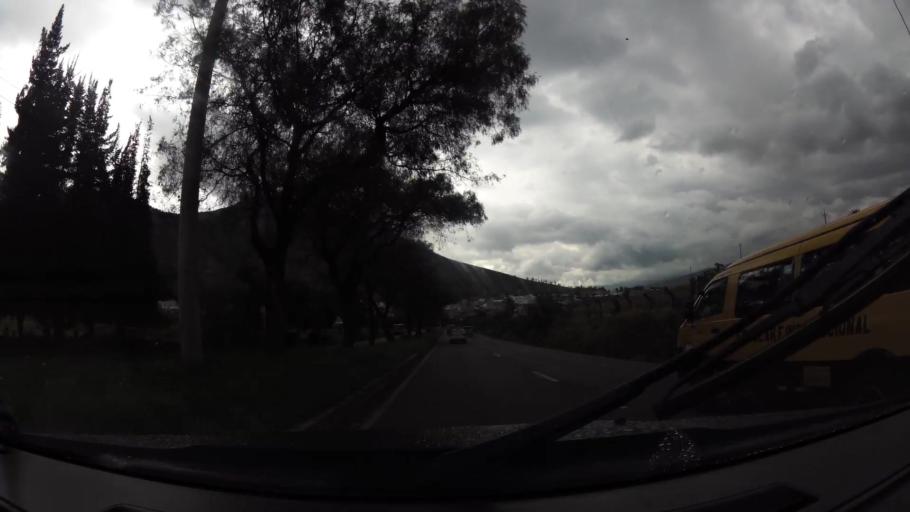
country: EC
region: Pichincha
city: Quito
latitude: -0.0788
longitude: -78.4811
